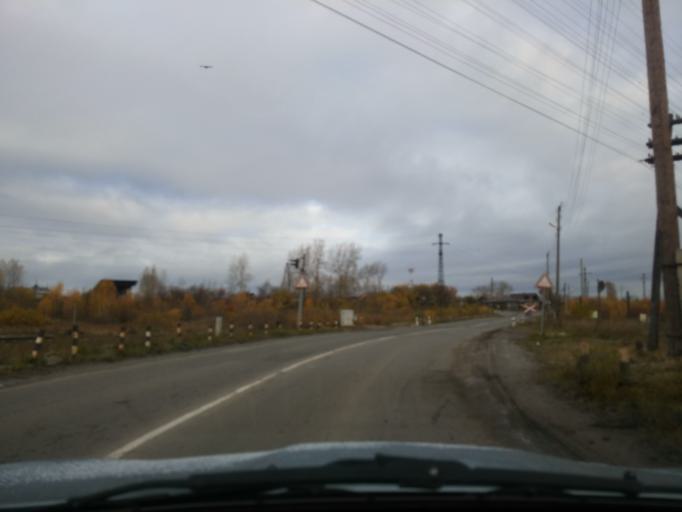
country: RU
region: Sverdlovsk
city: Turinsk
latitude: 58.0302
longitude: 63.7030
